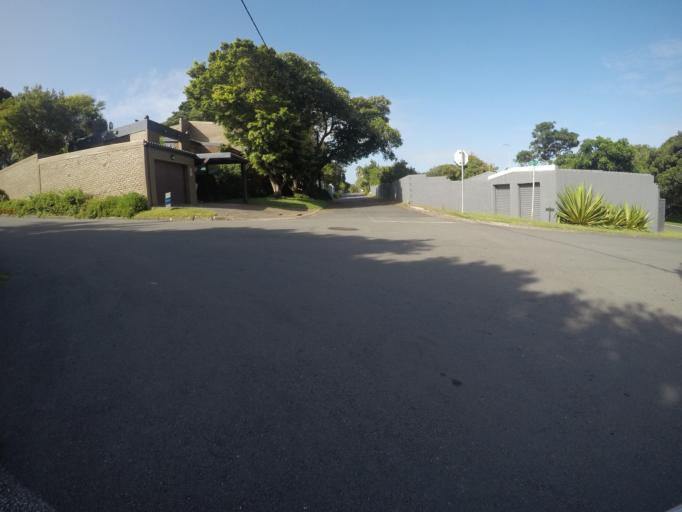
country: ZA
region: Eastern Cape
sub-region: Buffalo City Metropolitan Municipality
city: East London
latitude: -32.9754
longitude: 27.9580
